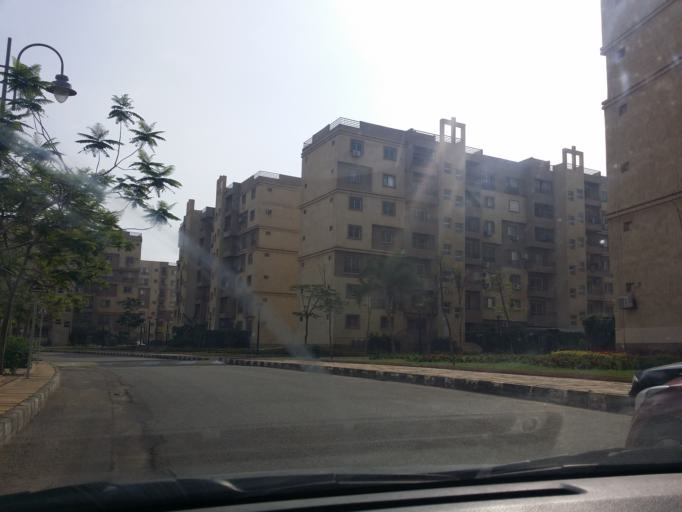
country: EG
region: Muhafazat al Qalyubiyah
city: Al Khankah
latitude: 30.0786
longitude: 31.6440
